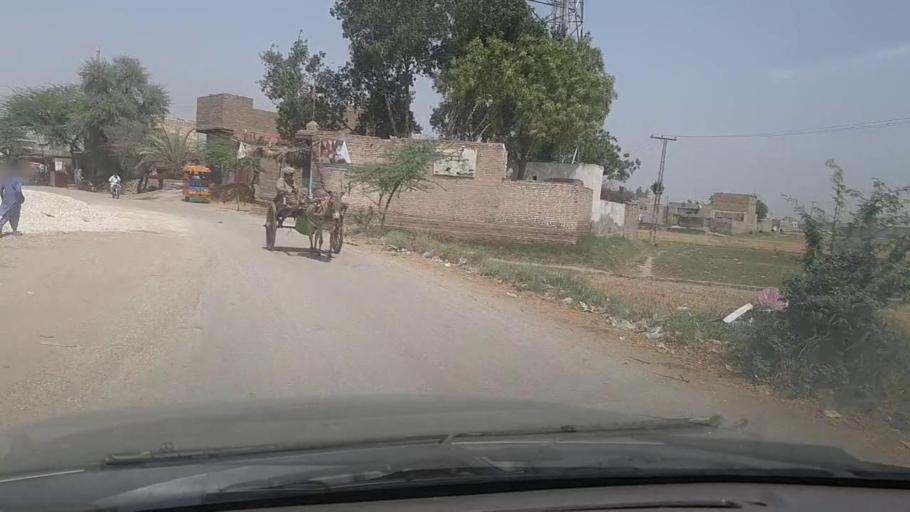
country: PK
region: Sindh
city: Madeji
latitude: 27.7993
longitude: 68.4072
